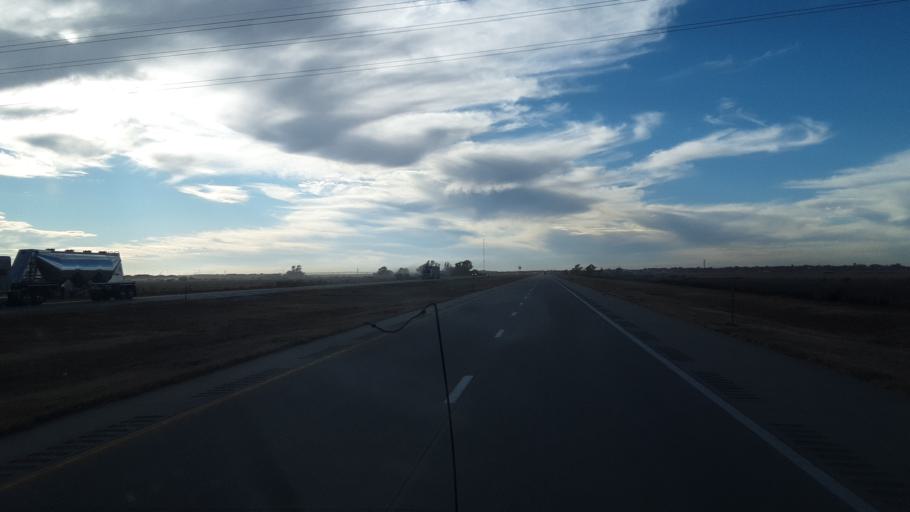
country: US
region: Kansas
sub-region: Finney County
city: Holcomb
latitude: 38.0034
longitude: -100.9657
